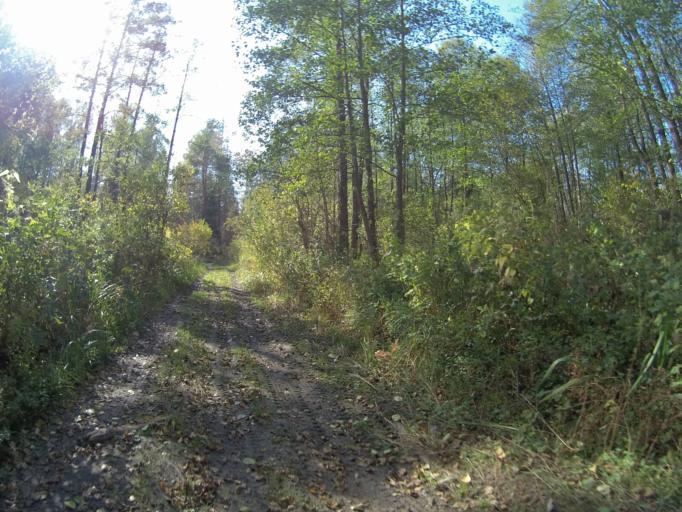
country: RU
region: Vladimir
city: Sobinka
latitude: 55.9185
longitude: 40.0587
